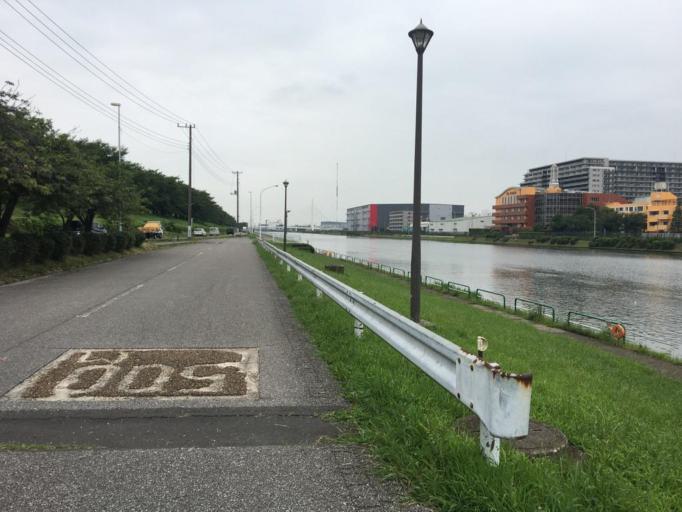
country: JP
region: Saitama
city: Shimotoda
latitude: 35.8025
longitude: 139.6717
